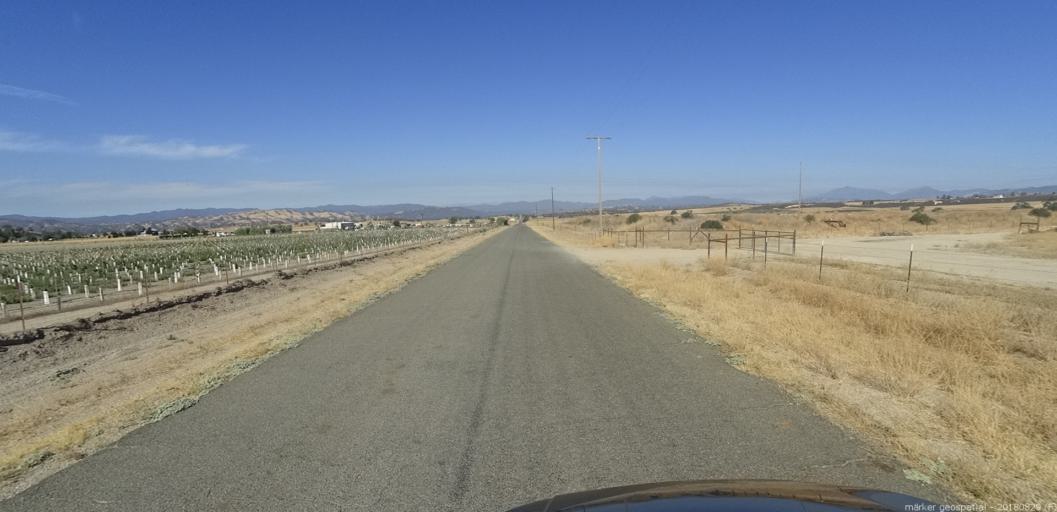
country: US
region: California
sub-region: Monterey County
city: King City
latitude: 35.9662
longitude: -121.0970
